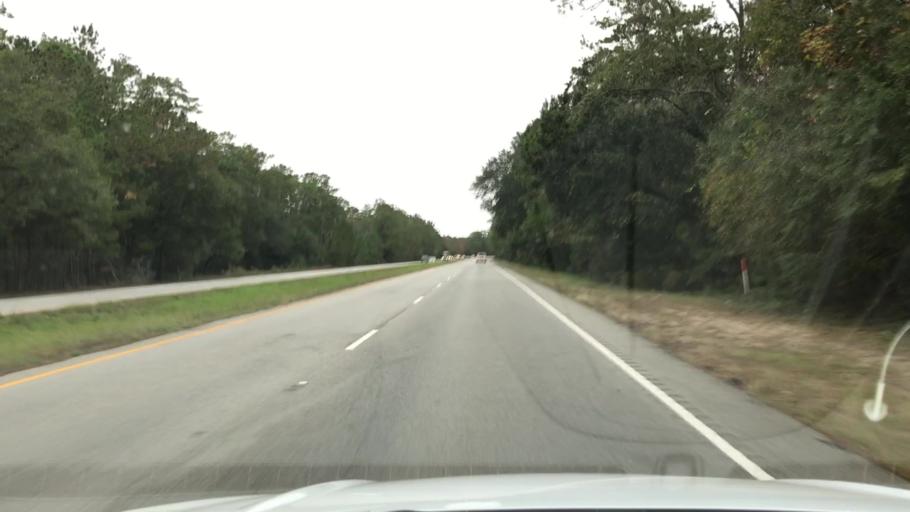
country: US
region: South Carolina
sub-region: Georgetown County
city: Georgetown
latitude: 33.3980
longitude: -79.2013
